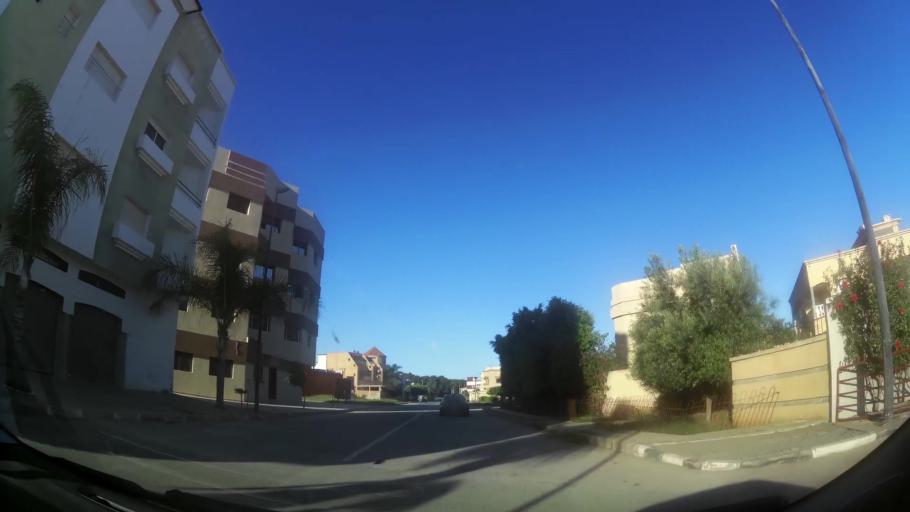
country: MA
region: Oriental
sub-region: Berkane-Taourirt
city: Madagh
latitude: 35.0866
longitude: -2.2476
